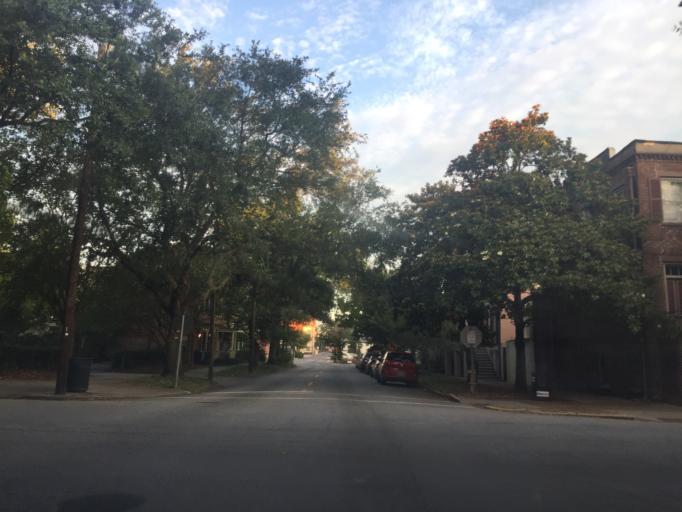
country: US
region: Georgia
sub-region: Chatham County
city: Savannah
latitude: 32.0707
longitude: -81.0972
